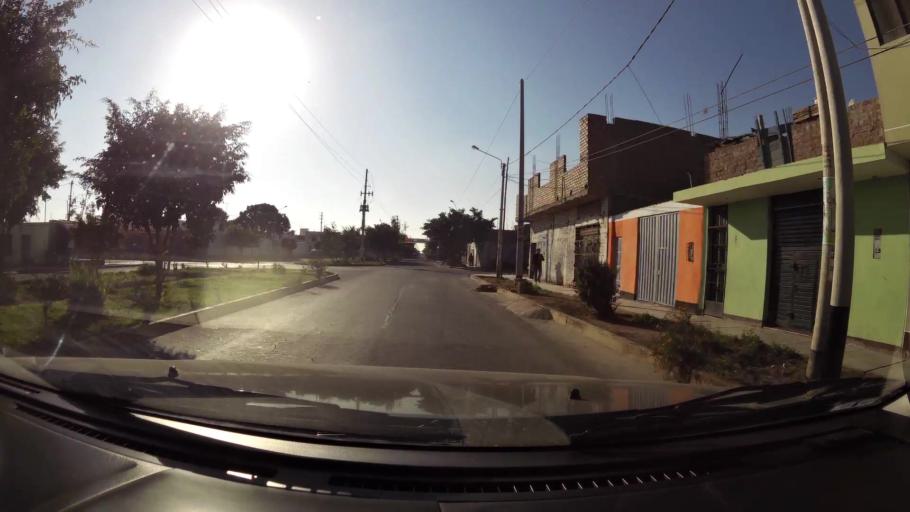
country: PE
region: Ica
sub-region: Provincia de Ica
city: La Tinguina
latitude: -14.0500
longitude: -75.6983
